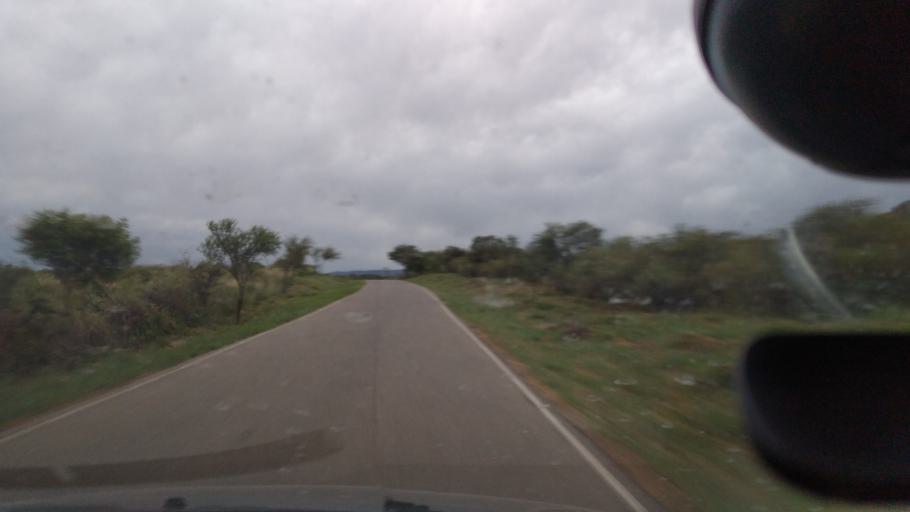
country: AR
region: Cordoba
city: Villa Las Rosas
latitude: -31.8849
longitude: -65.0256
